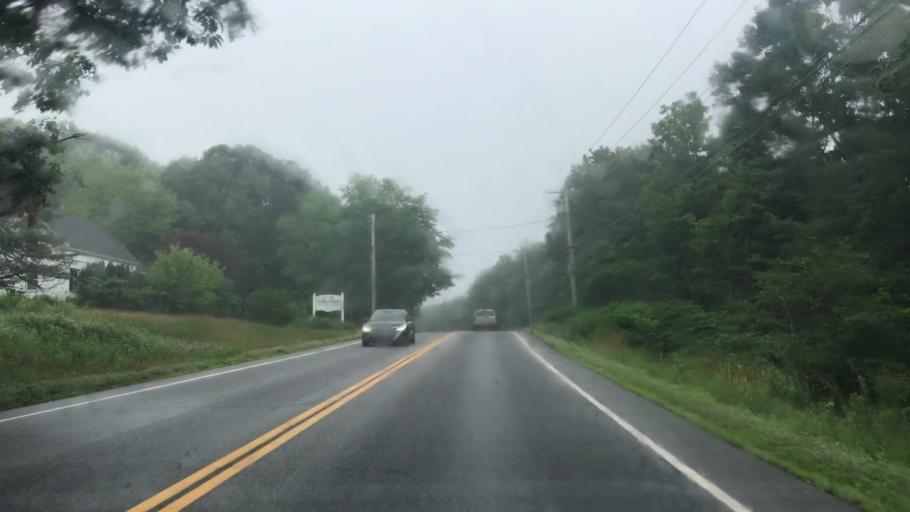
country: US
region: Maine
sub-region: Lincoln County
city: Boothbay
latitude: 43.8951
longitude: -69.6280
